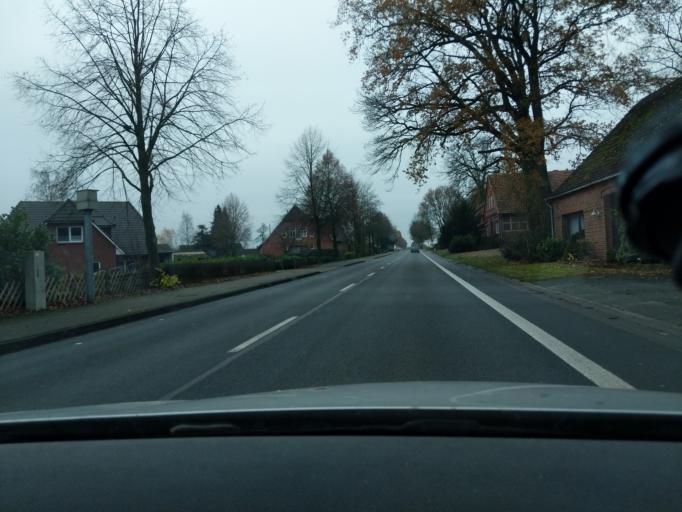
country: DE
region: Lower Saxony
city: Zeven
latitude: 53.2592
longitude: 9.2794
